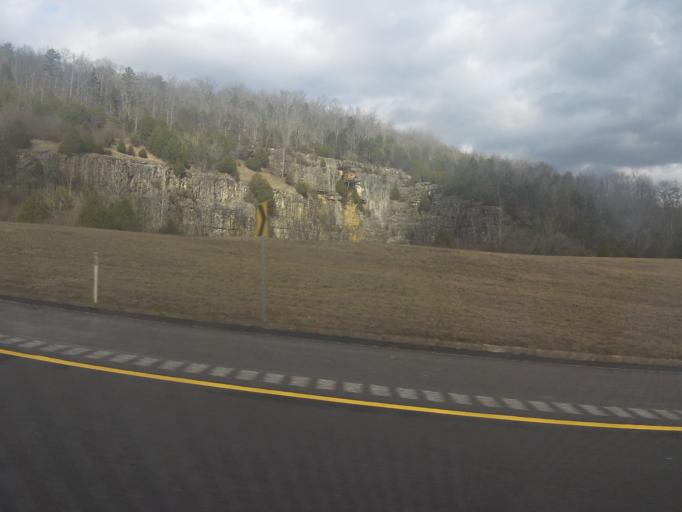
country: US
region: Tennessee
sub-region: Marion County
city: Monteagle
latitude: 35.1756
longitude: -85.7996
